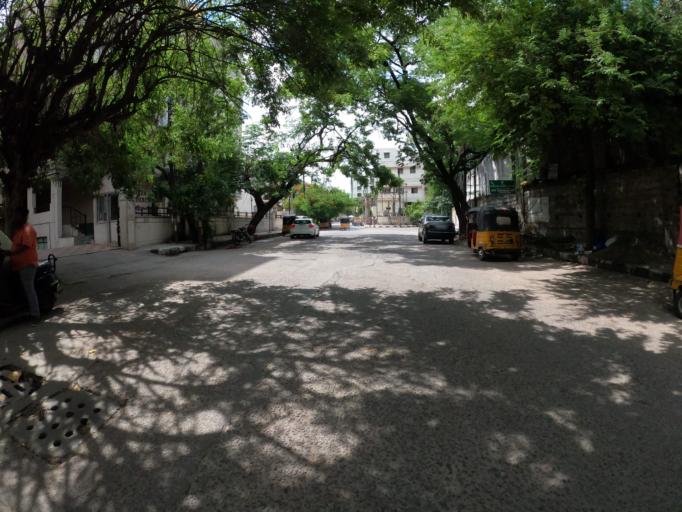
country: IN
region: Telangana
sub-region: Hyderabad
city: Hyderabad
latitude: 17.4017
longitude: 78.4582
